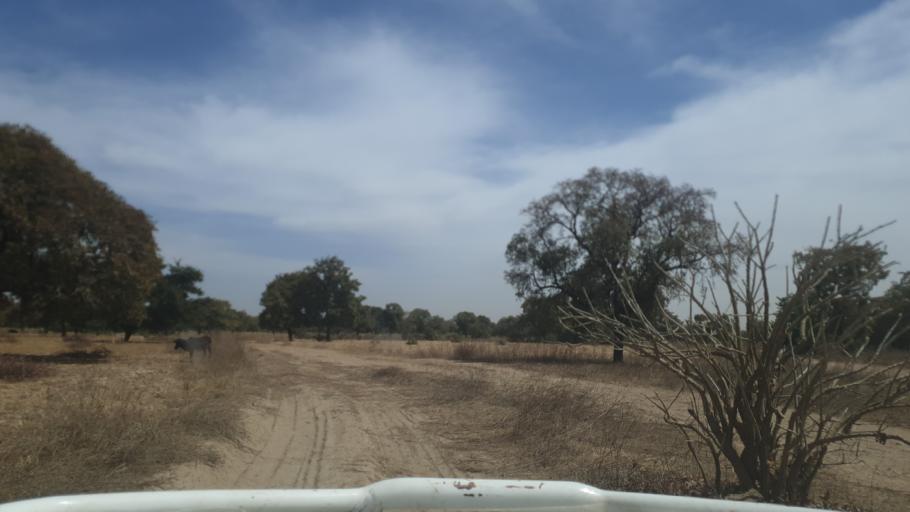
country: ML
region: Sikasso
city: Yorosso
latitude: 12.2855
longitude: -4.6803
